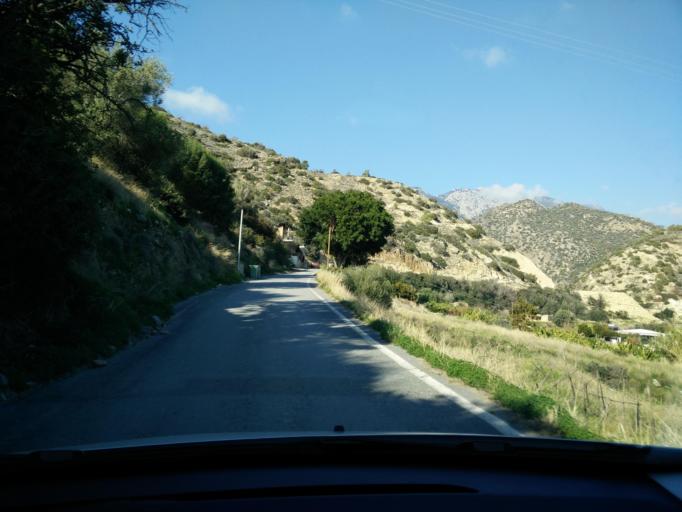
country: GR
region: Crete
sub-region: Nomos Lasithiou
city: Gra Liyia
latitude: 34.9923
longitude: 25.5323
